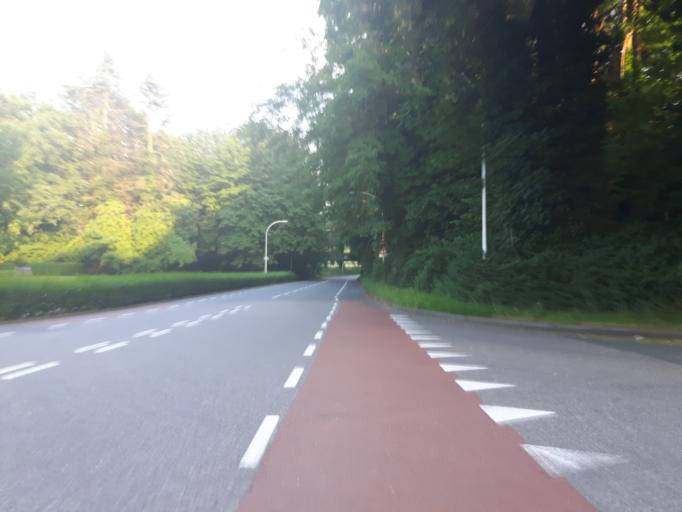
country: NL
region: Overijssel
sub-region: Gemeente Hengelo
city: Hengelo
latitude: 52.2491
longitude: 6.8021
